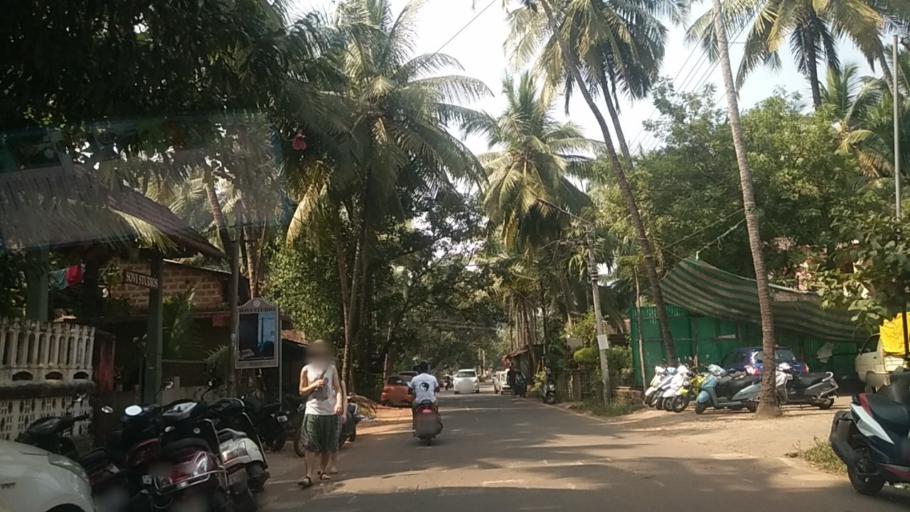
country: IN
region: Goa
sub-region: North Goa
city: Arambol
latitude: 15.6672
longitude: 73.7215
